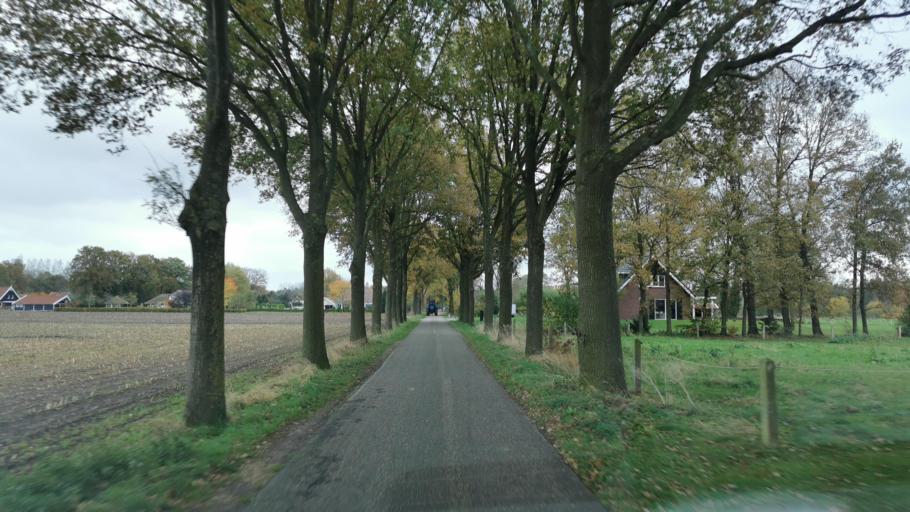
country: DE
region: North Rhine-Westphalia
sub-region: Regierungsbezirk Munster
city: Gronau
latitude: 52.2396
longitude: 7.0530
